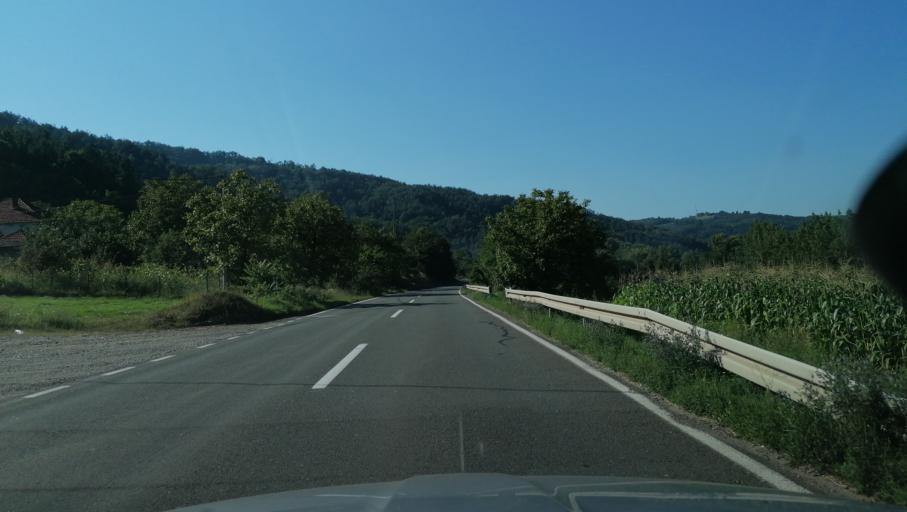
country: RS
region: Central Serbia
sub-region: Raski Okrug
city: Kraljevo
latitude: 43.6717
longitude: 20.5769
